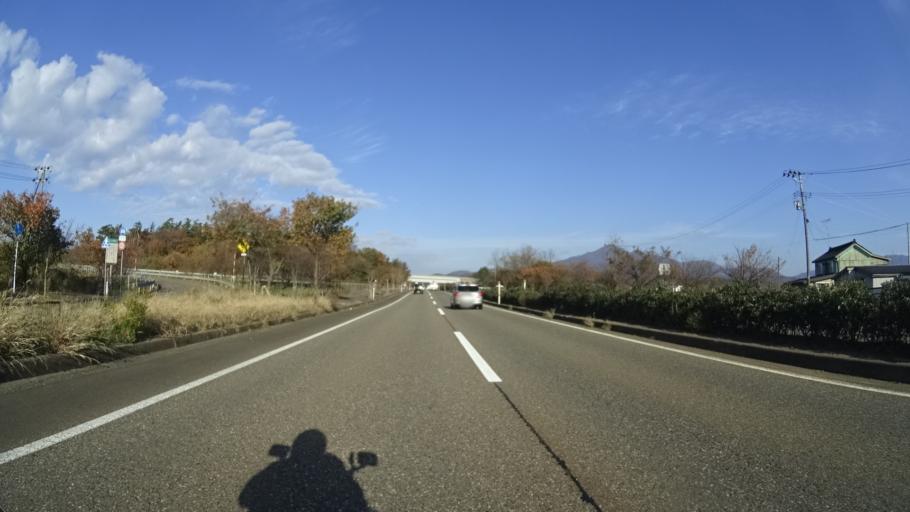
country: JP
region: Niigata
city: Kashiwazaki
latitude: 37.2698
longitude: 138.3864
